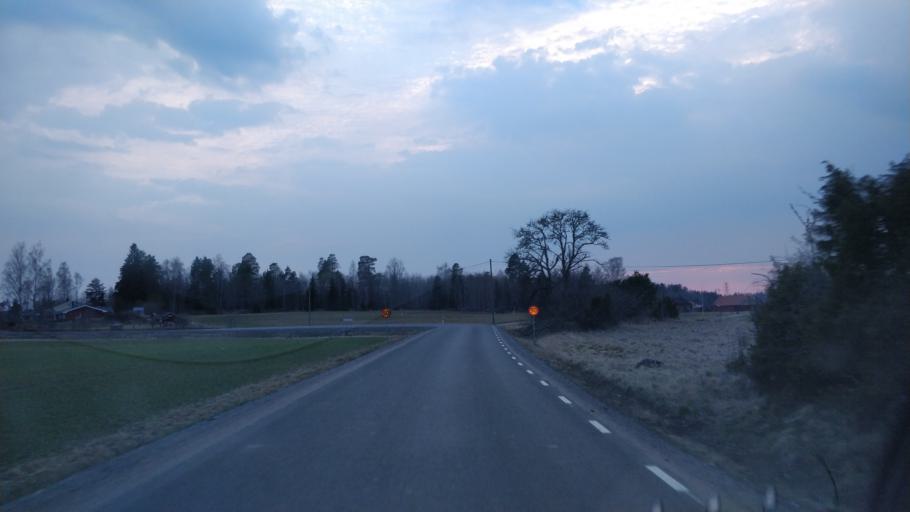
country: SE
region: Uppsala
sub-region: Enkopings Kommun
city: Orsundsbro
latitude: 59.7252
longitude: 17.2741
